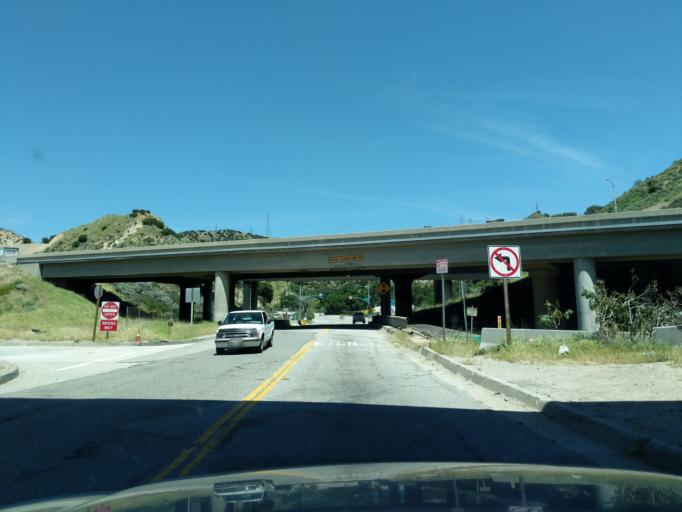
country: US
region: California
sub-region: Los Angeles County
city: Santa Clarita
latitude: 34.3332
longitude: -118.5056
